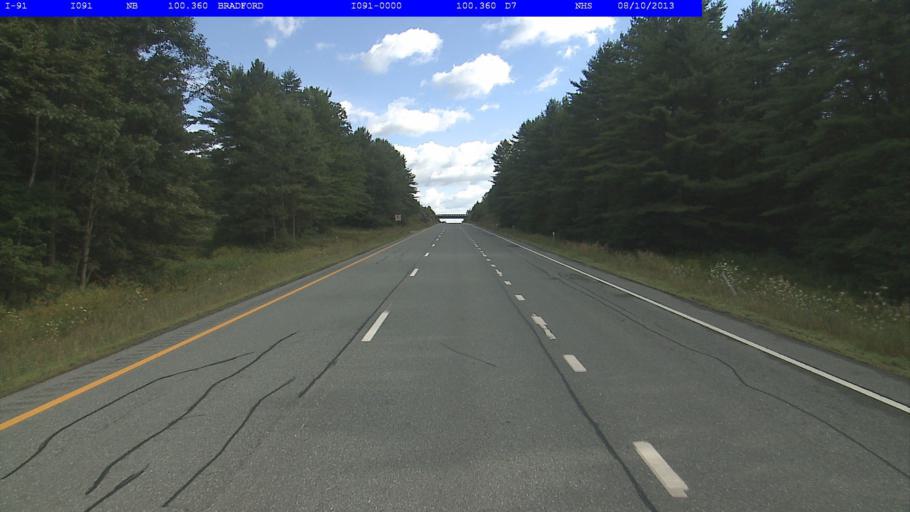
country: US
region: New Hampshire
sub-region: Grafton County
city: Haverhill
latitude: 44.0200
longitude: -72.1185
